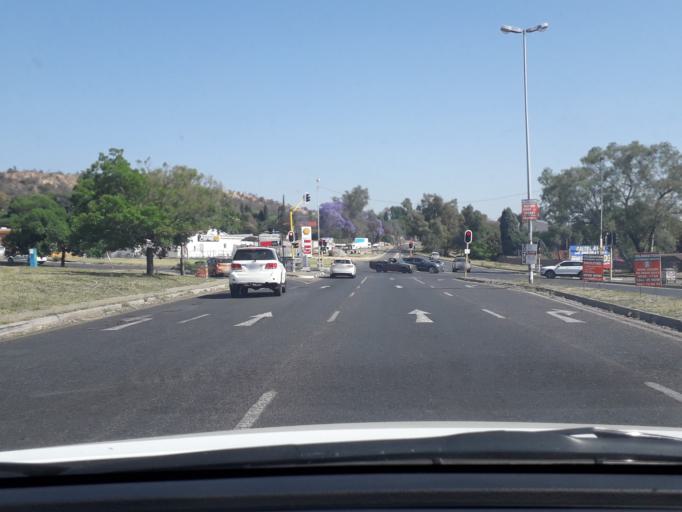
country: ZA
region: Gauteng
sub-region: City of Johannesburg Metropolitan Municipality
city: Roodepoort
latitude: -26.0923
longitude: 27.9605
